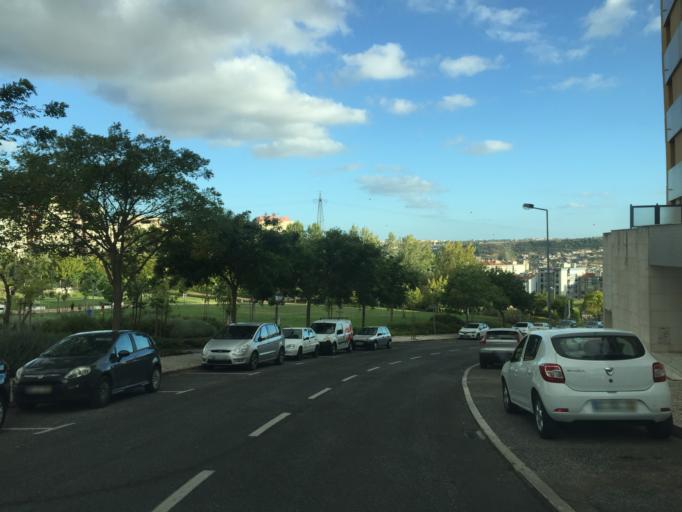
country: PT
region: Lisbon
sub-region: Odivelas
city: Odivelas
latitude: 38.7994
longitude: -9.1838
